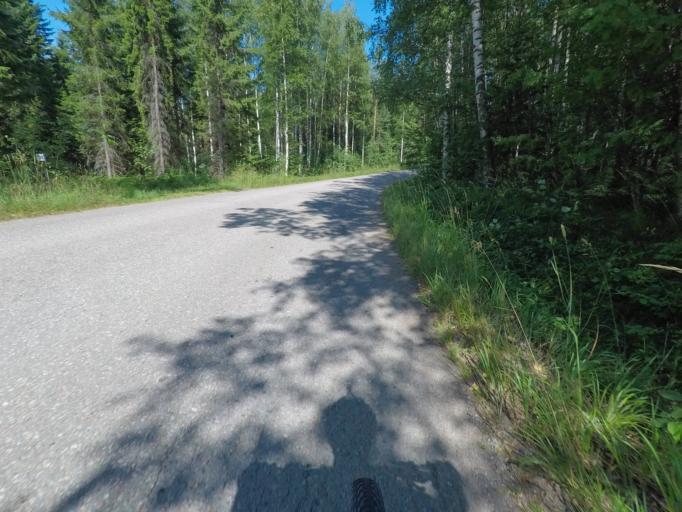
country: FI
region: Southern Savonia
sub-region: Mikkeli
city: Puumala
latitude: 61.4208
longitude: 28.1196
